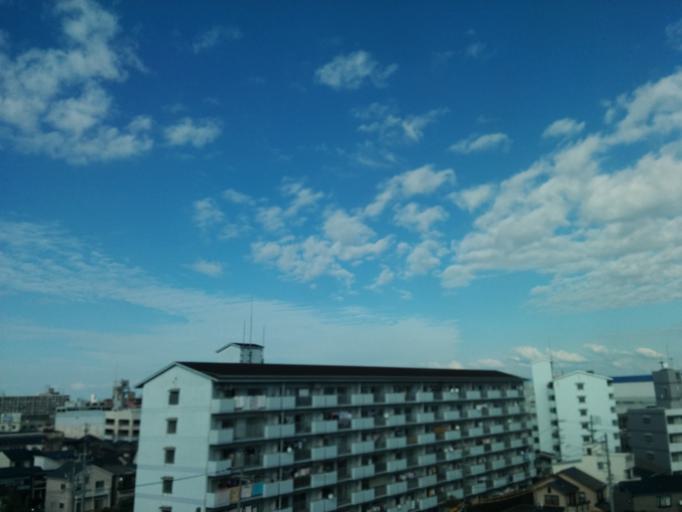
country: JP
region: Aichi
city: Nagoya-shi
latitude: 35.1057
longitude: 136.9171
